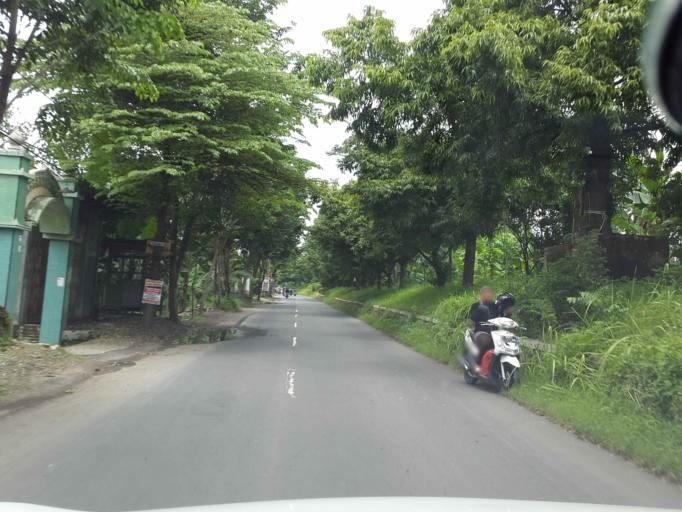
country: ID
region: East Java
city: Mojokerto
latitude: -7.4582
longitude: 112.4228
